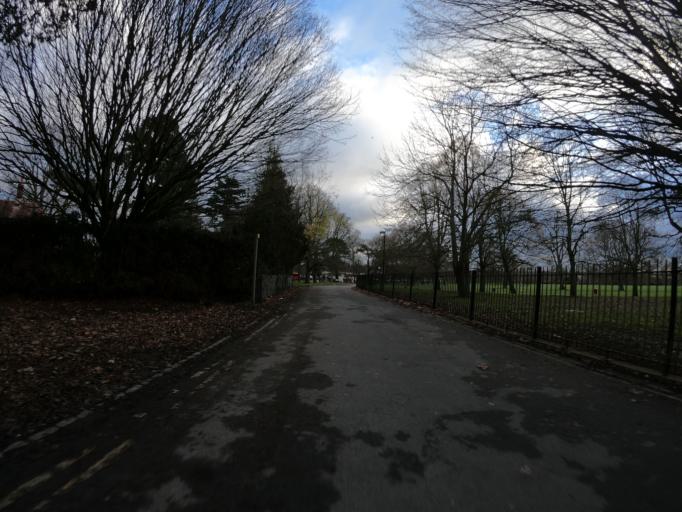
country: GB
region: England
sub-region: Greater London
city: Welling
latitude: 51.4503
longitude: 0.0795
